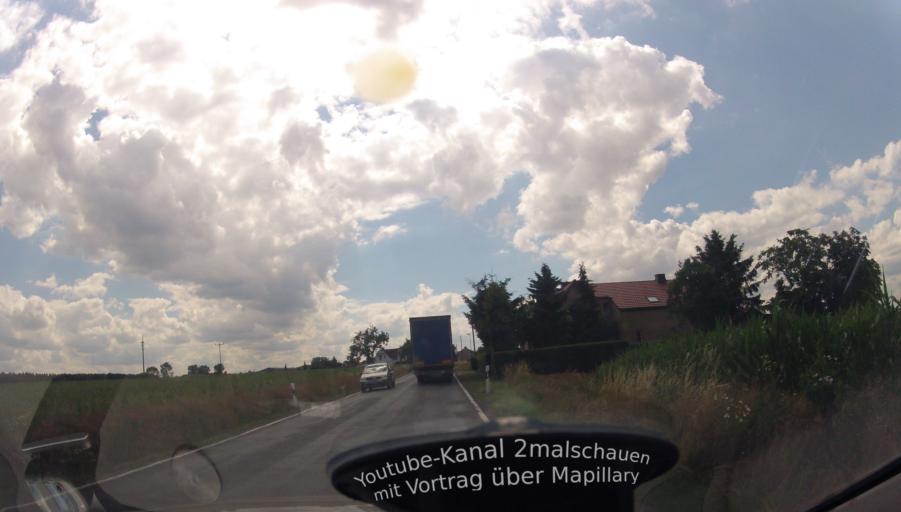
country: DE
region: Saxony
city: Schildau
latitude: 51.4922
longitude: 12.9651
